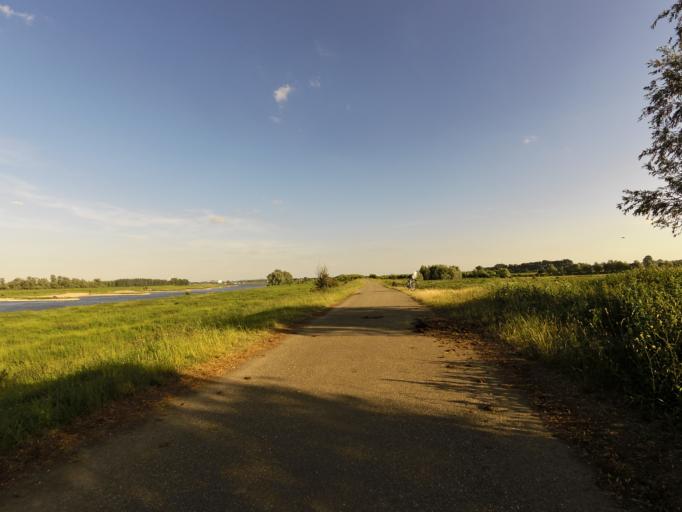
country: NL
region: Gelderland
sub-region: Gemeente Duiven
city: Duiven
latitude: 51.8874
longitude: 6.0237
